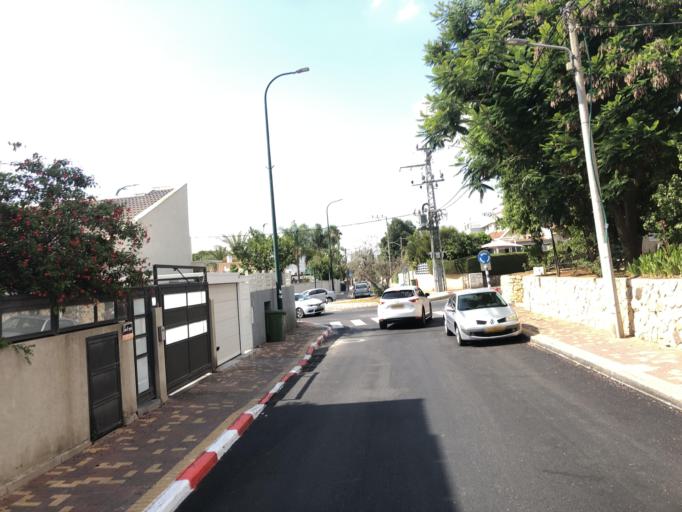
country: IL
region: Central District
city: Yehud
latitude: 32.0382
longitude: 34.8843
